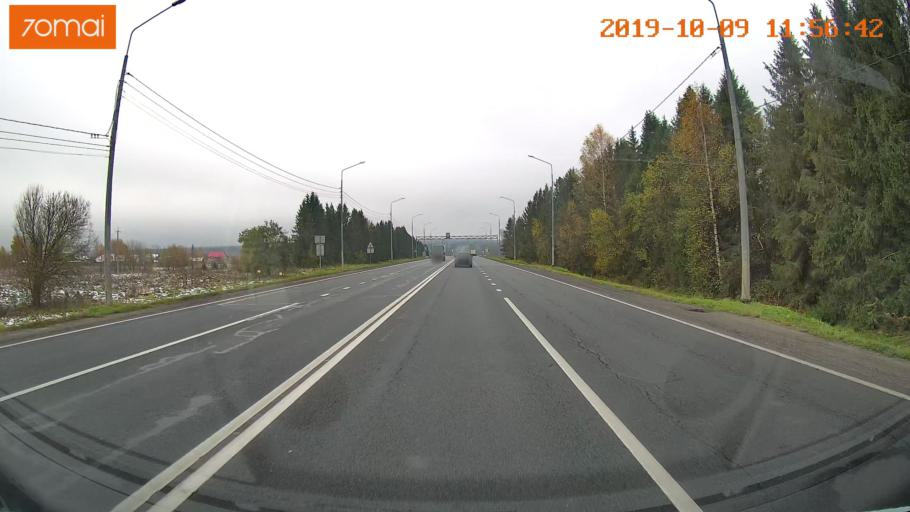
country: RU
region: Vologda
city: Gryazovets
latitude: 58.7412
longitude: 40.2888
